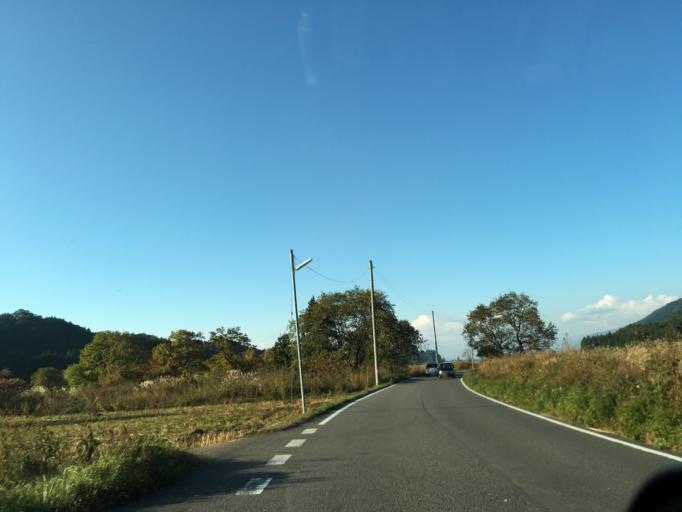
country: JP
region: Fukushima
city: Inawashiro
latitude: 37.4042
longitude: 140.1457
